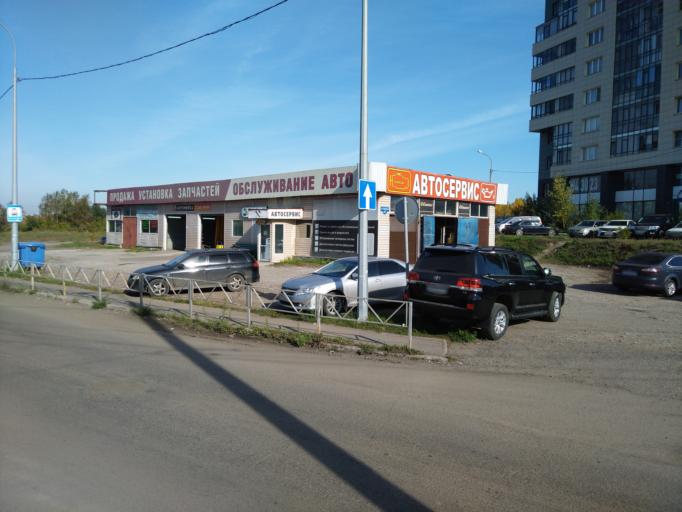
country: RU
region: Krasnoyarskiy
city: Krasnoyarsk
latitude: 56.0156
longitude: 92.9578
